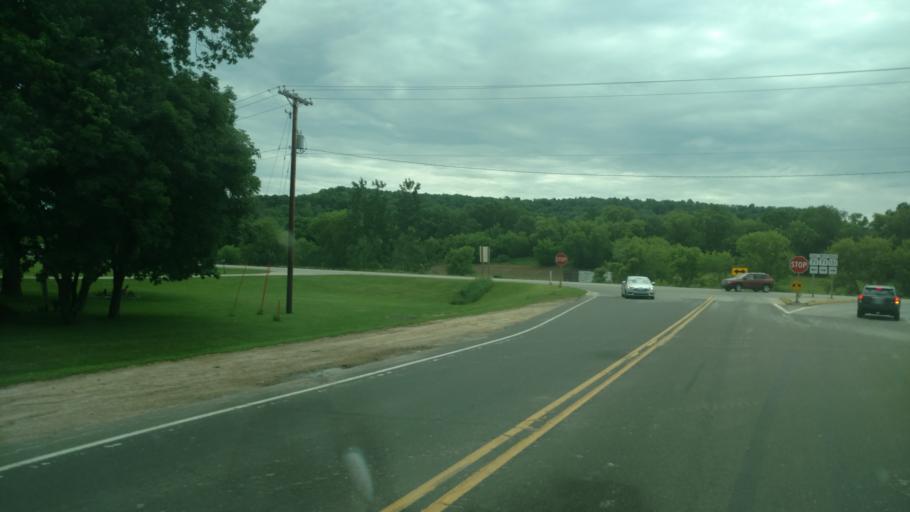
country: US
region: Wisconsin
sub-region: Monroe County
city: Tomah
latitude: 43.8334
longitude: -90.4740
